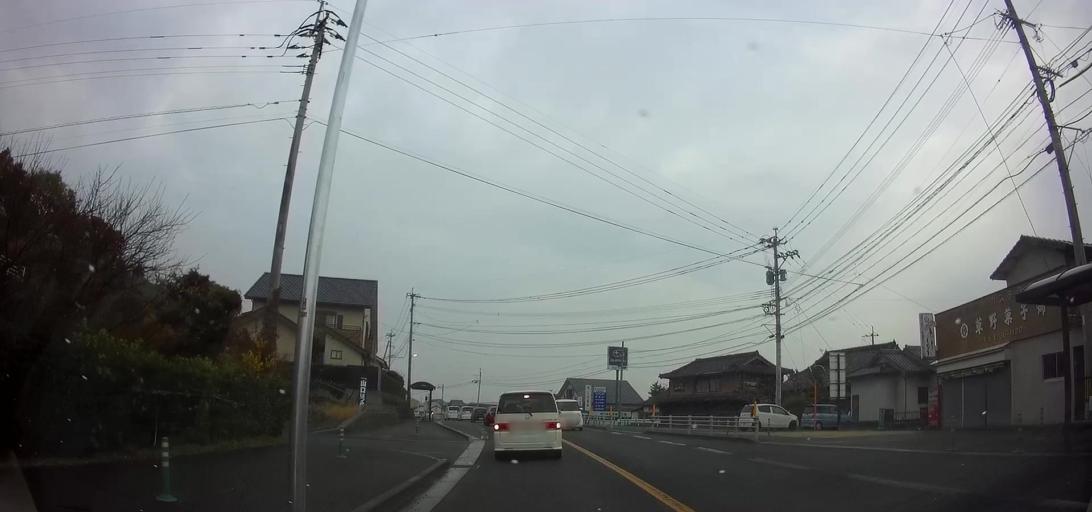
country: JP
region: Nagasaki
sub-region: Isahaya-shi
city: Isahaya
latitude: 32.8337
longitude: 130.1348
